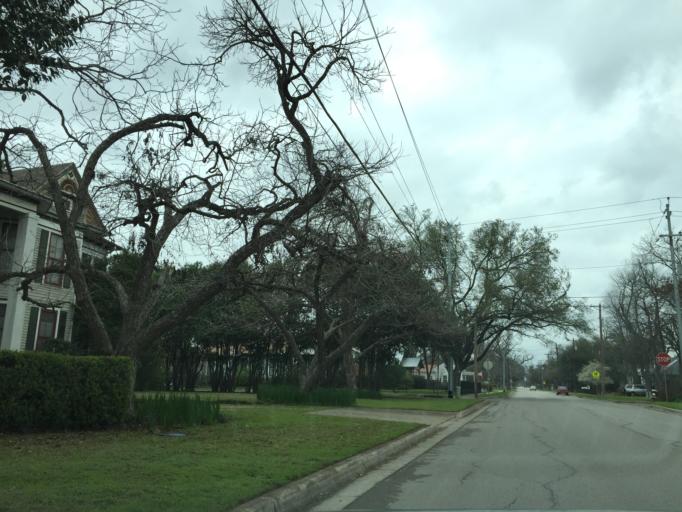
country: US
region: Texas
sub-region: Bastrop County
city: Bastrop
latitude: 30.1112
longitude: -97.3176
